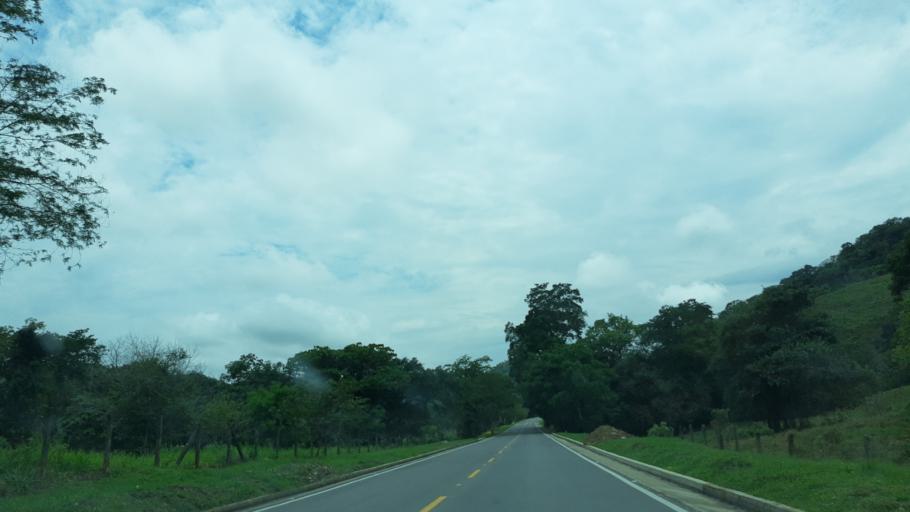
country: CO
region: Boyaca
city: San Luis de Gaceno
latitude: 4.8301
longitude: -73.1440
